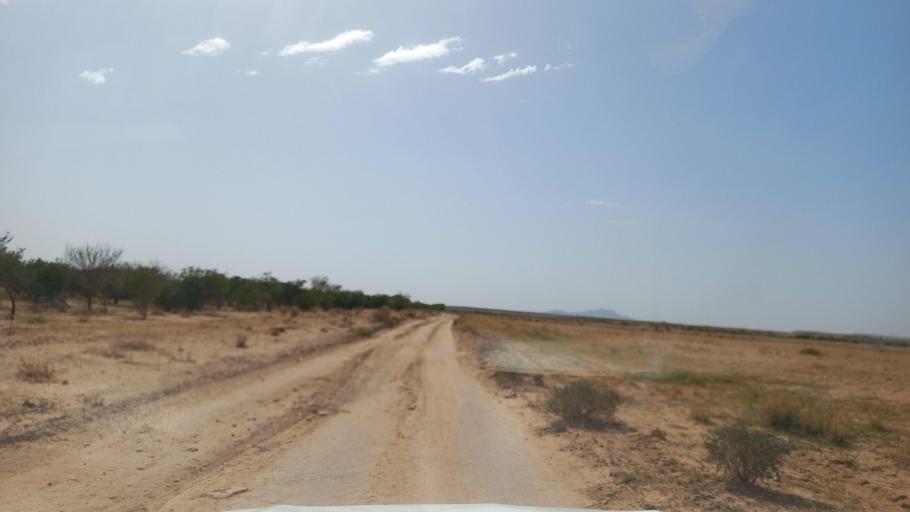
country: TN
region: Al Qasrayn
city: Kasserine
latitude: 35.2558
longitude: 8.9634
